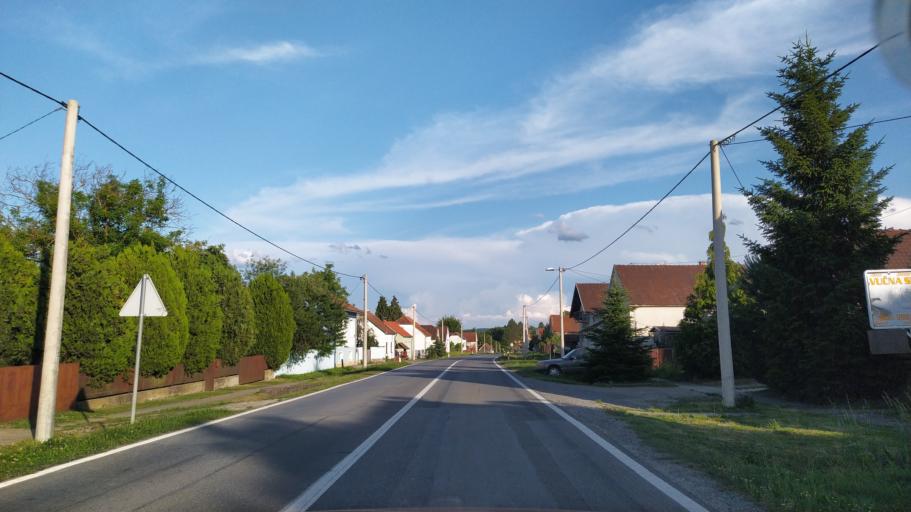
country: HR
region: Virovitick-Podravska
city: Cacinci
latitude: 45.6366
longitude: 17.7928
